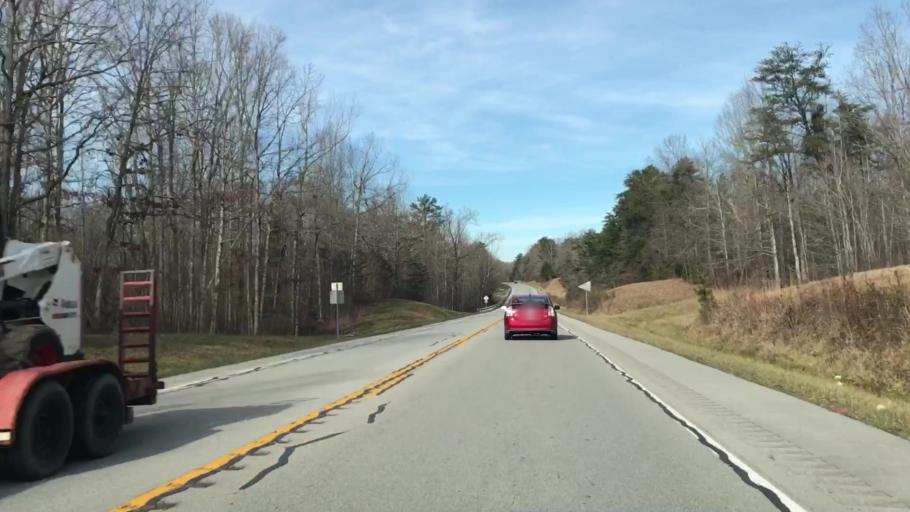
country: US
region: Kentucky
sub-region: McCreary County
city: Whitley City
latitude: 36.7704
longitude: -84.4789
